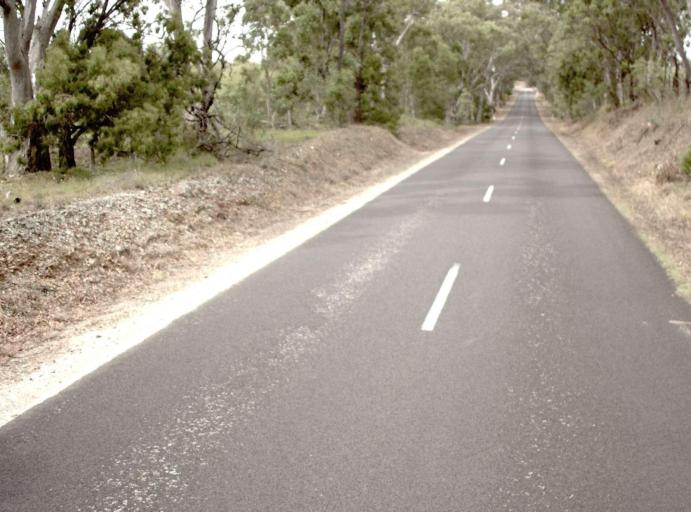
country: AU
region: Victoria
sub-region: Wellington
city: Sale
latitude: -37.8811
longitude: 147.0651
